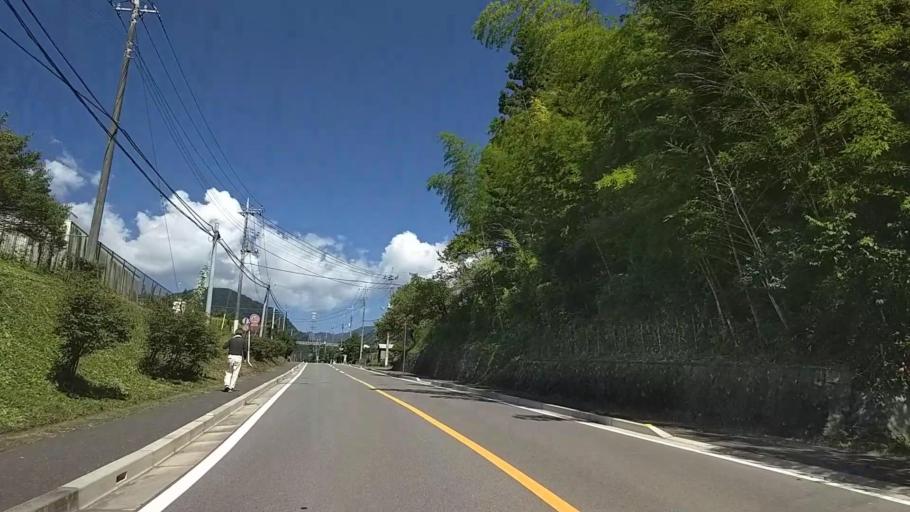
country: JP
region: Gunma
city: Annaka
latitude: 36.3402
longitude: 138.7270
